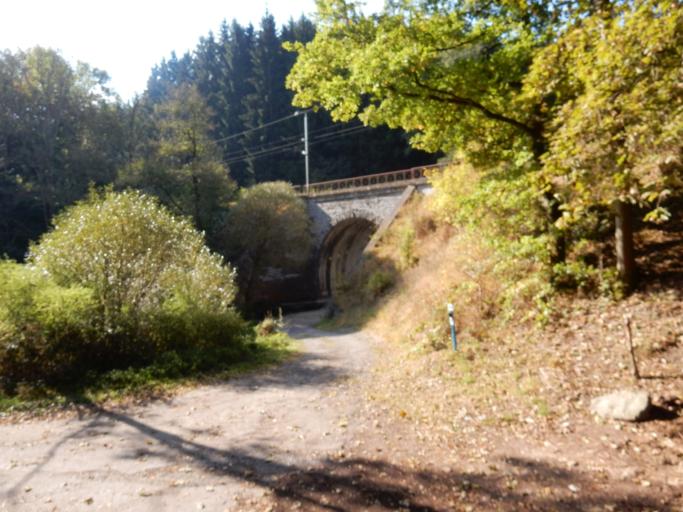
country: LU
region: Diekirch
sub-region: Canton de Clervaux
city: Clervaux
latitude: 50.0478
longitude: 6.0186
